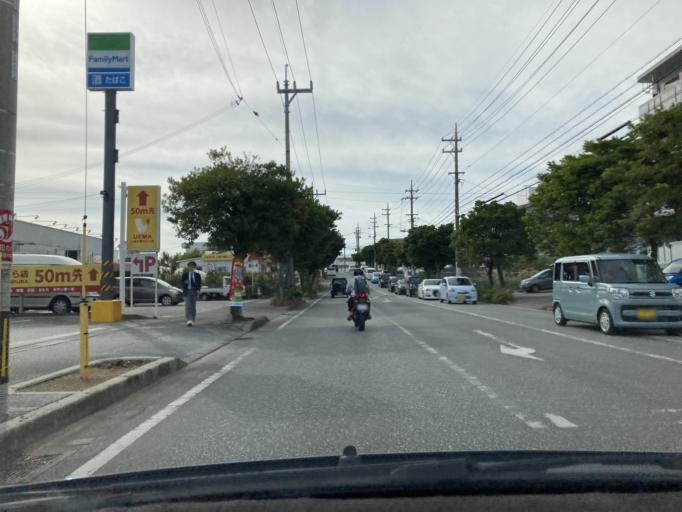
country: JP
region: Okinawa
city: Okinawa
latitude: 26.3457
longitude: 127.8308
